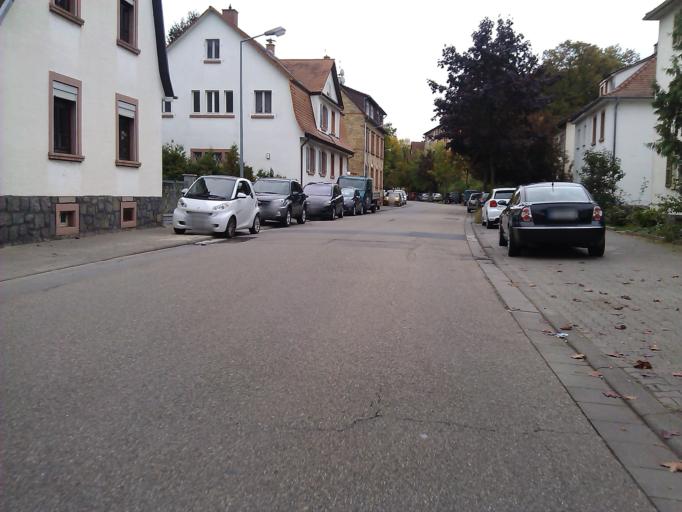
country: DE
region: Baden-Wuerttemberg
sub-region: Karlsruhe Region
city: Weinheim
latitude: 49.5553
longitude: 8.6589
